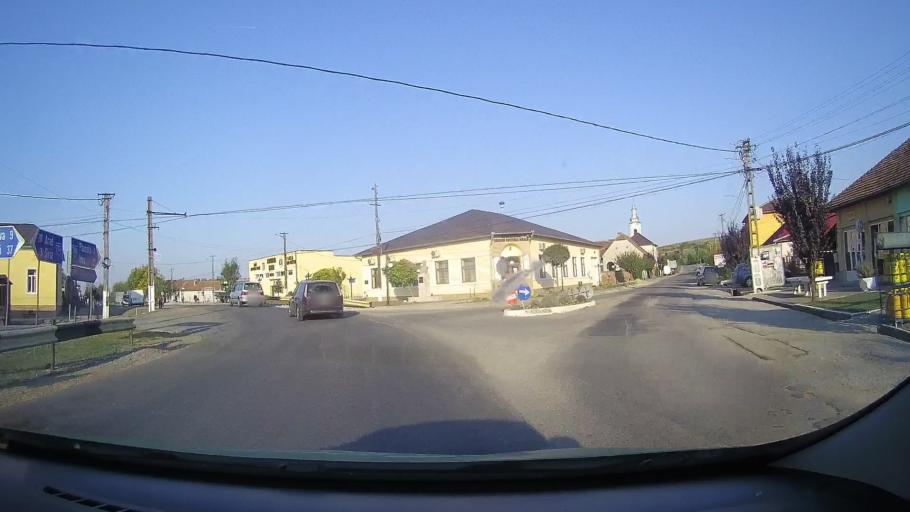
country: RO
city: Masca
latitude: 46.2963
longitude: 21.6704
